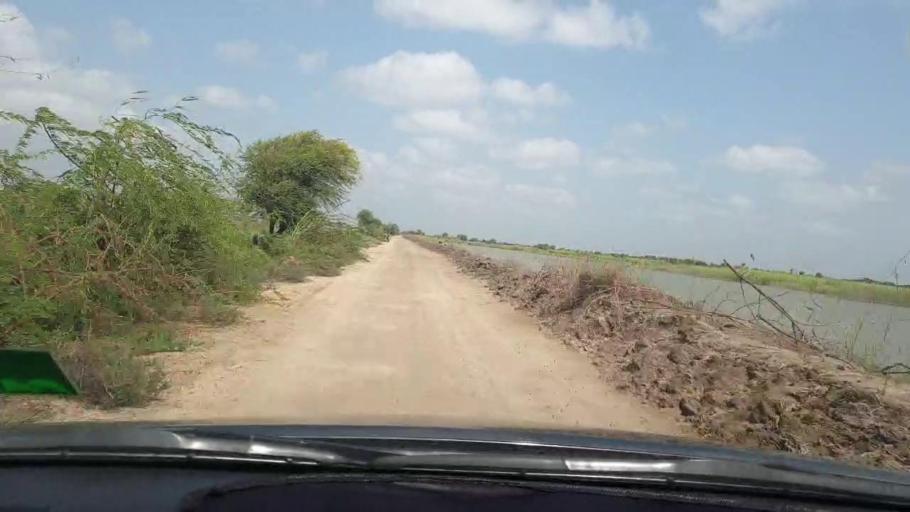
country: PK
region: Sindh
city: Tando Bago
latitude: 24.8593
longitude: 69.0354
